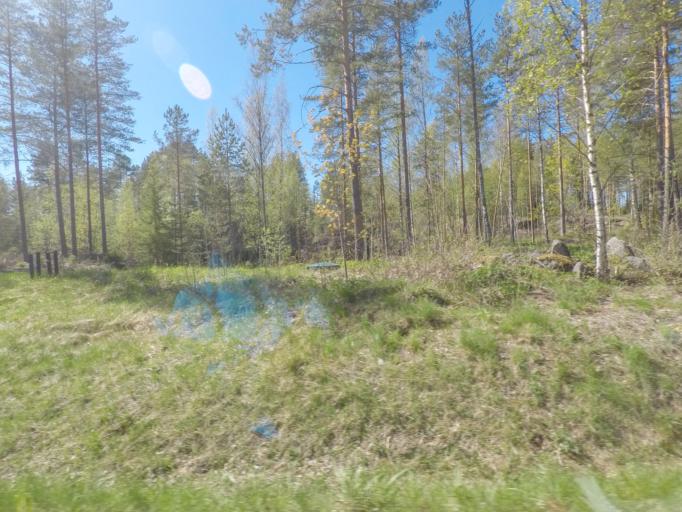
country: FI
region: Uusimaa
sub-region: Helsinki
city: Sammatti
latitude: 60.3298
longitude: 23.8132
